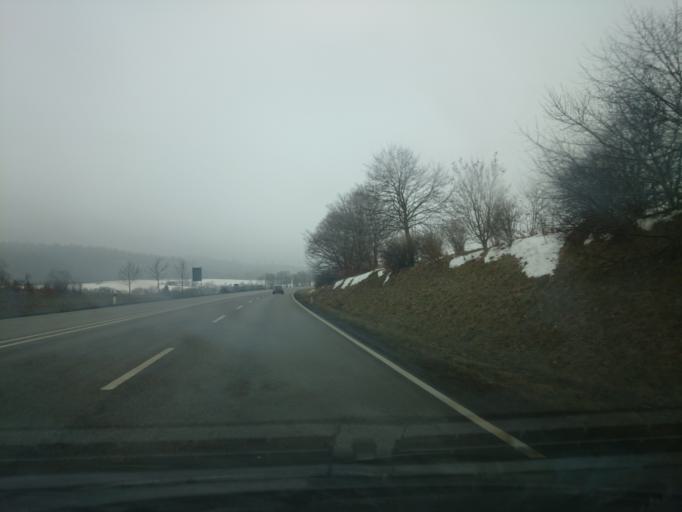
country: DE
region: Bavaria
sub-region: Swabia
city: Kuhbach
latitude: 48.4923
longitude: 11.2035
